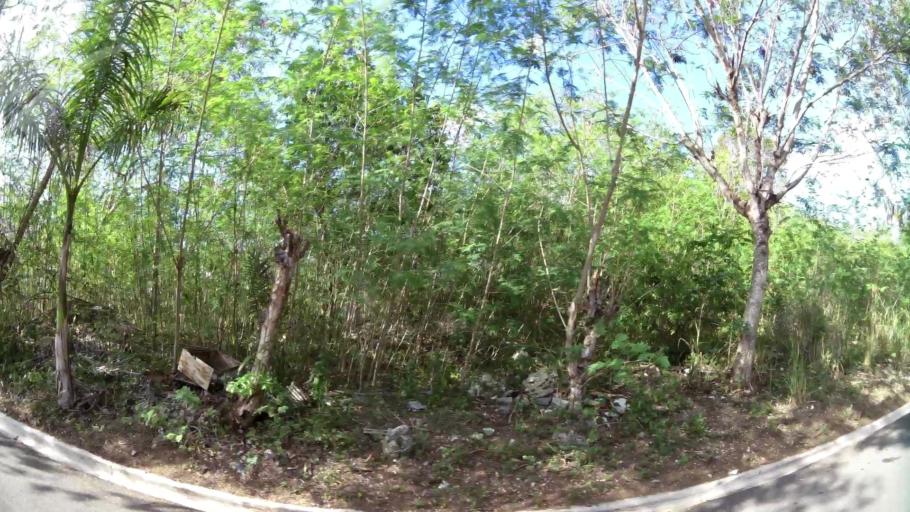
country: DO
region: Nacional
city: Santo Domingo
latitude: 18.5114
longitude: -69.9752
